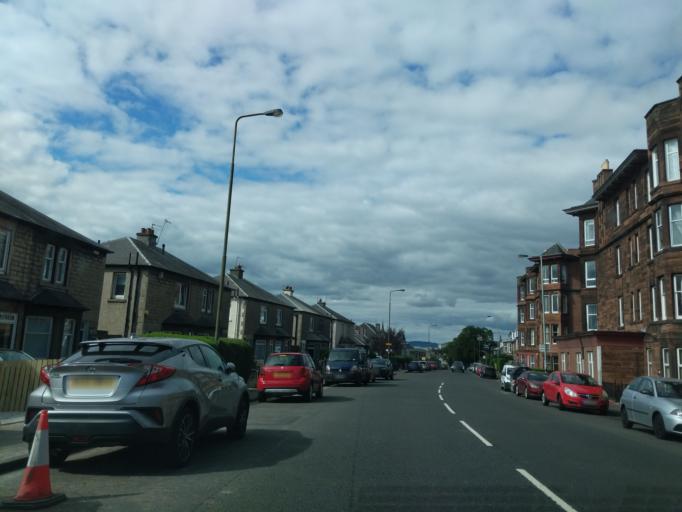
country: GB
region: Scotland
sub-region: West Lothian
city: Seafield
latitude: 55.9651
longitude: -3.1630
